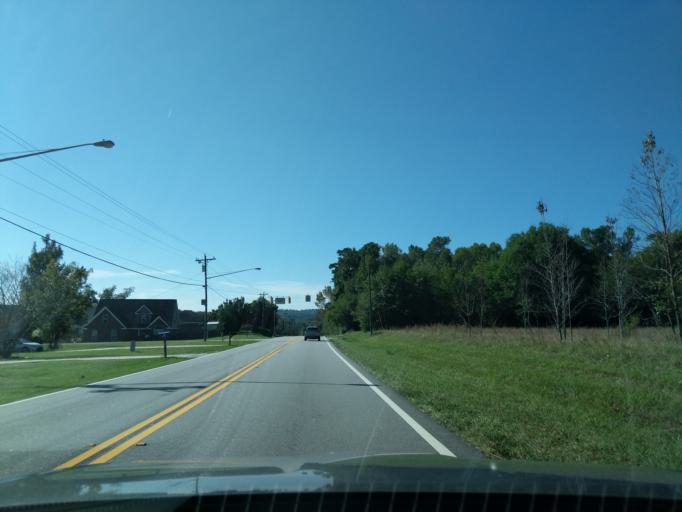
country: US
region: Georgia
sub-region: Richmond County
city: Hephzibah
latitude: 33.3528
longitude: -82.0002
